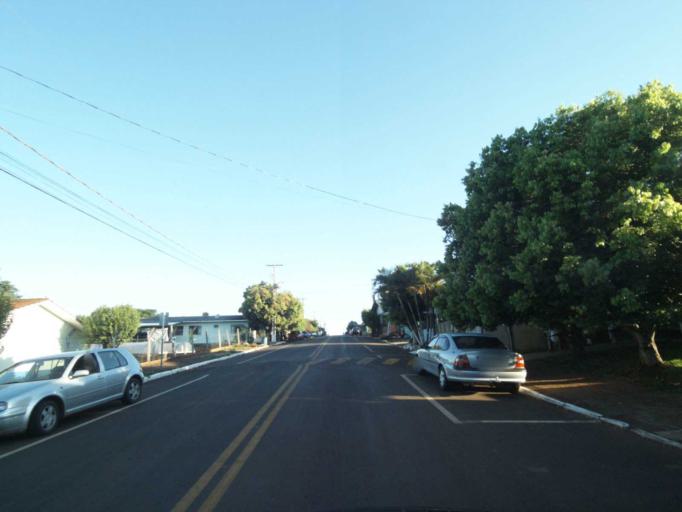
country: BR
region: Parana
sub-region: Coronel Vivida
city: Coronel Vivida
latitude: -25.9540
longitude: -52.8194
